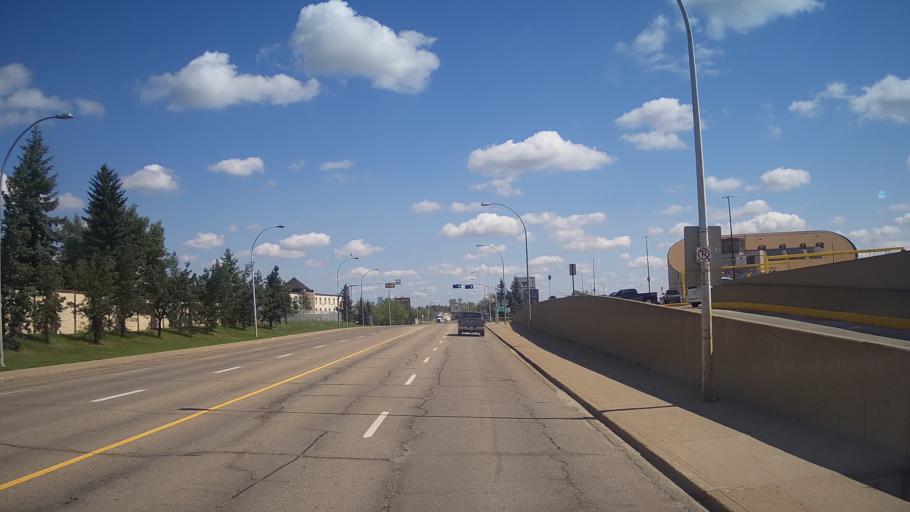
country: CA
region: Alberta
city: St. Albert
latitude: 53.5248
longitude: -113.6270
